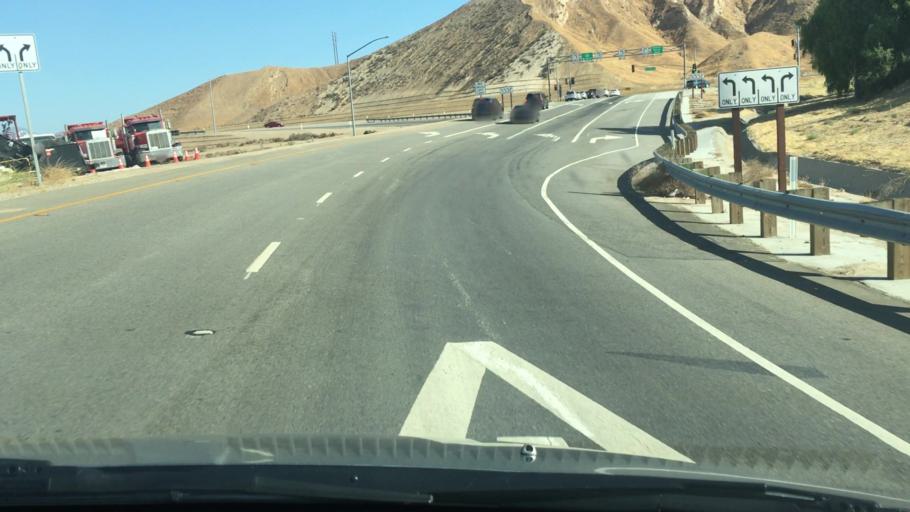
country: US
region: California
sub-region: Los Angeles County
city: Valencia
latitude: 34.4423
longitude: -118.6025
